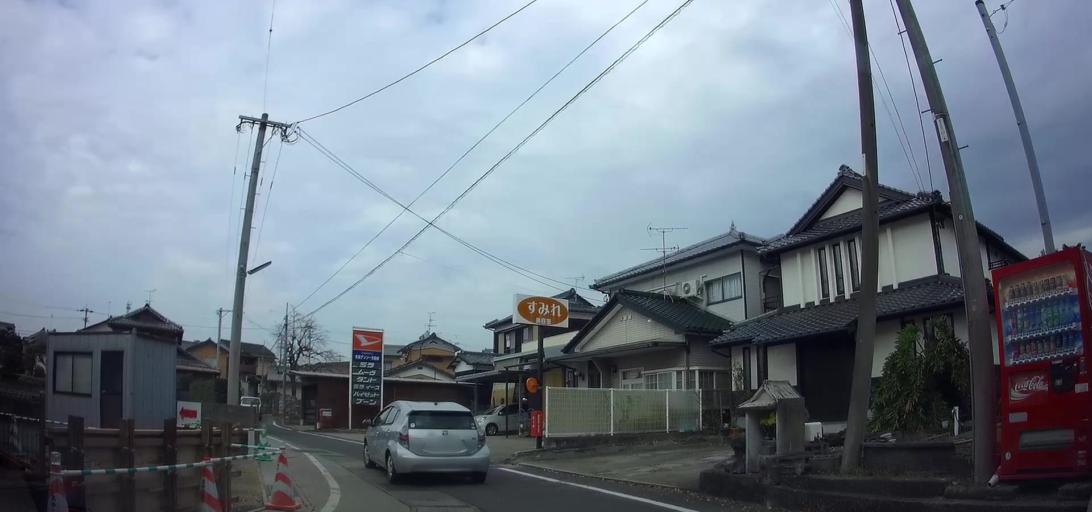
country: JP
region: Nagasaki
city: Shimabara
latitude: 32.6693
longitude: 130.3024
